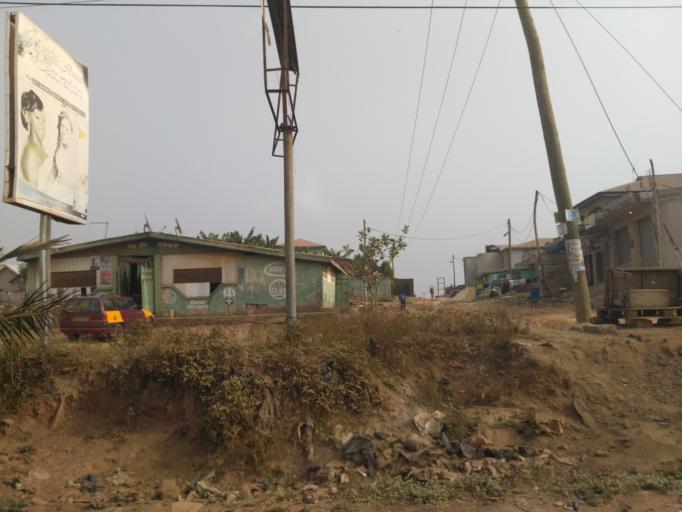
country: GH
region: Ashanti
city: Kumasi
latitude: 6.6472
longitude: -1.5809
